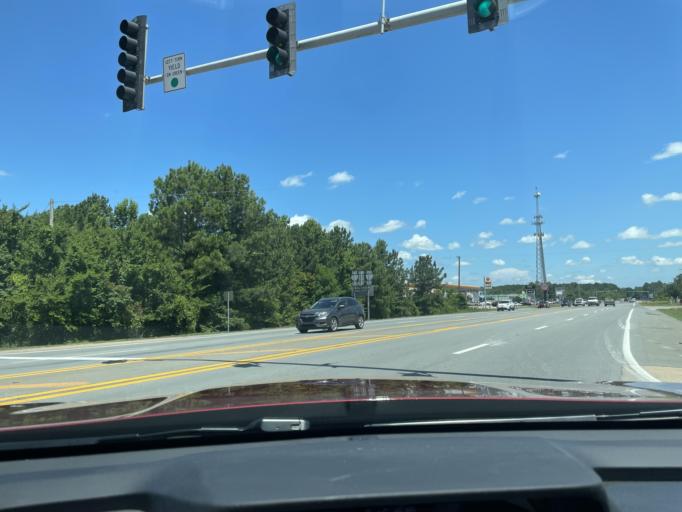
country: US
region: Arkansas
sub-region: Jefferson County
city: Pine Bluff
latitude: 34.1719
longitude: -92.0065
